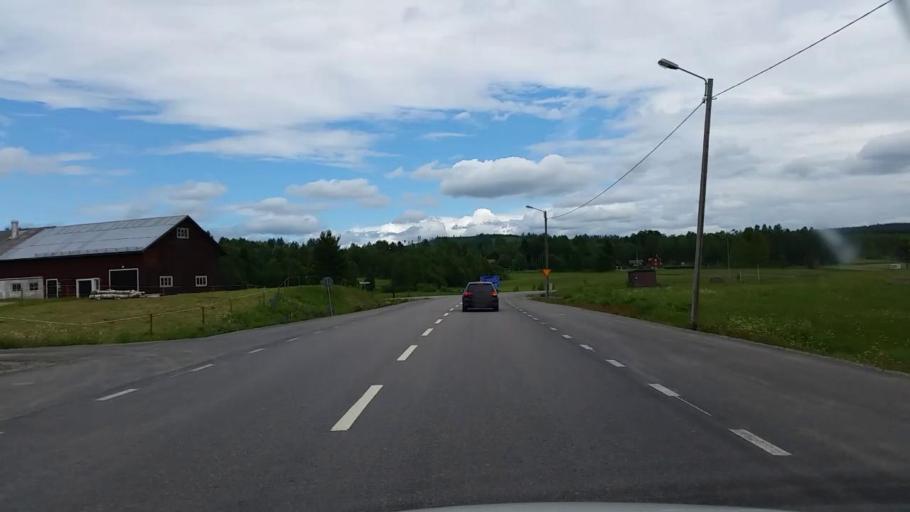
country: SE
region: Gaevleborg
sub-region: Ockelbo Kommun
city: Ockelbo
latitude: 60.9664
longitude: 16.4409
